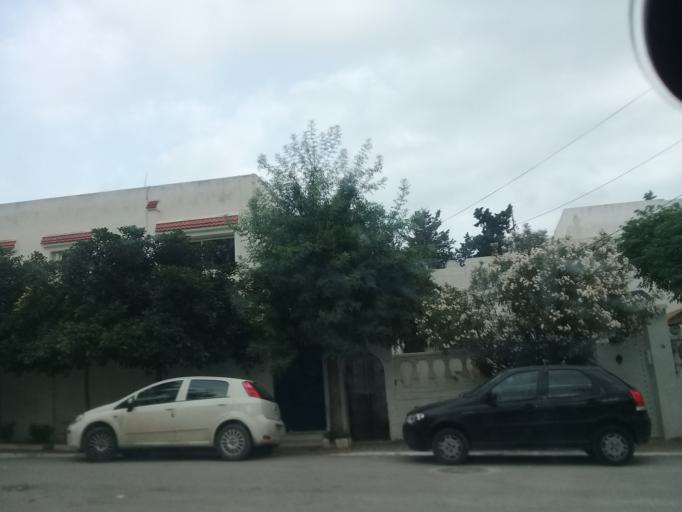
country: TN
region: Tunis
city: Sidi Bou Said
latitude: 36.8682
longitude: 10.3374
